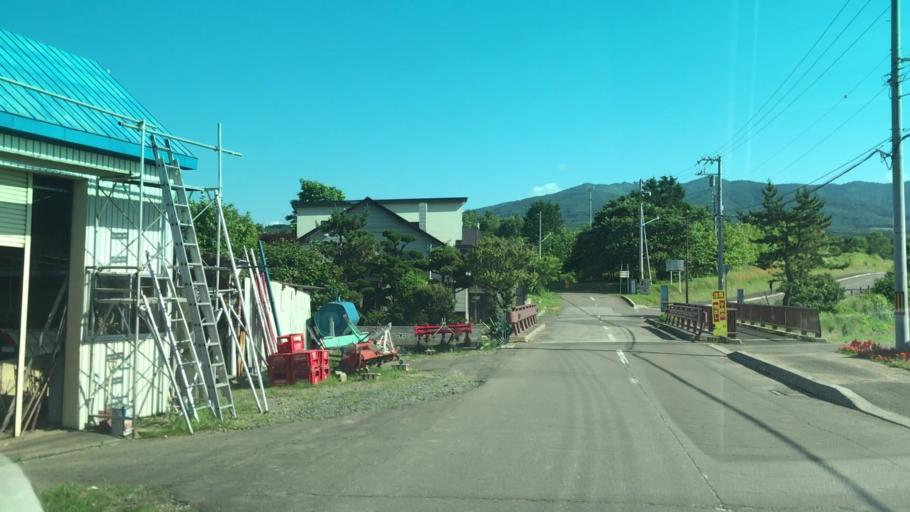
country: JP
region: Hokkaido
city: Iwanai
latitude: 42.9795
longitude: 140.6086
